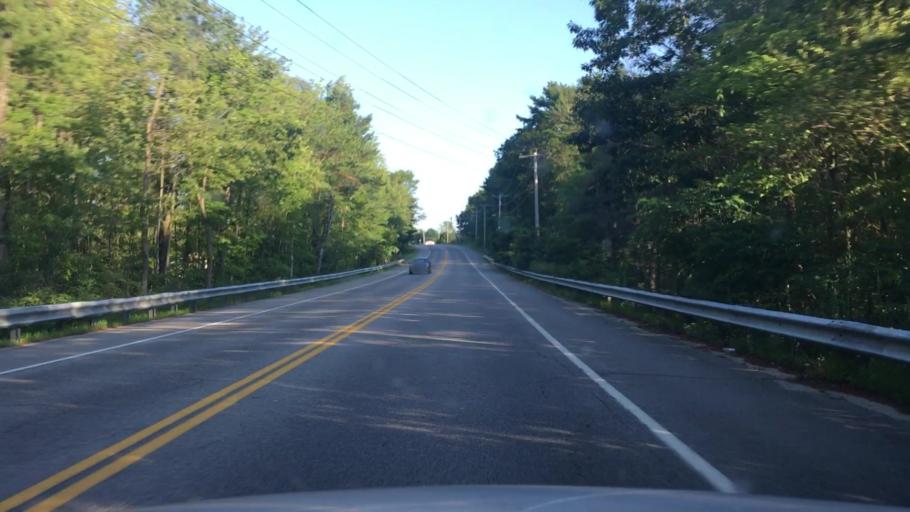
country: US
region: Maine
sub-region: Androscoggin County
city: Lisbon
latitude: 44.0274
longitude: -70.1021
